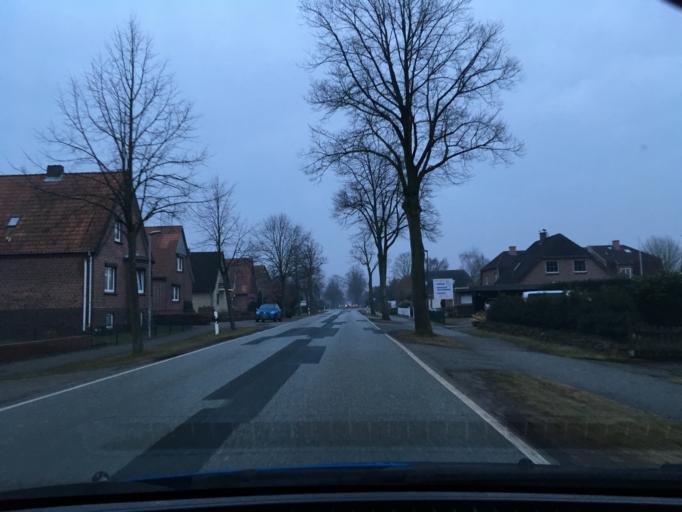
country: DE
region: Lower Saxony
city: Winsen
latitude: 53.3751
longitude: 10.1936
